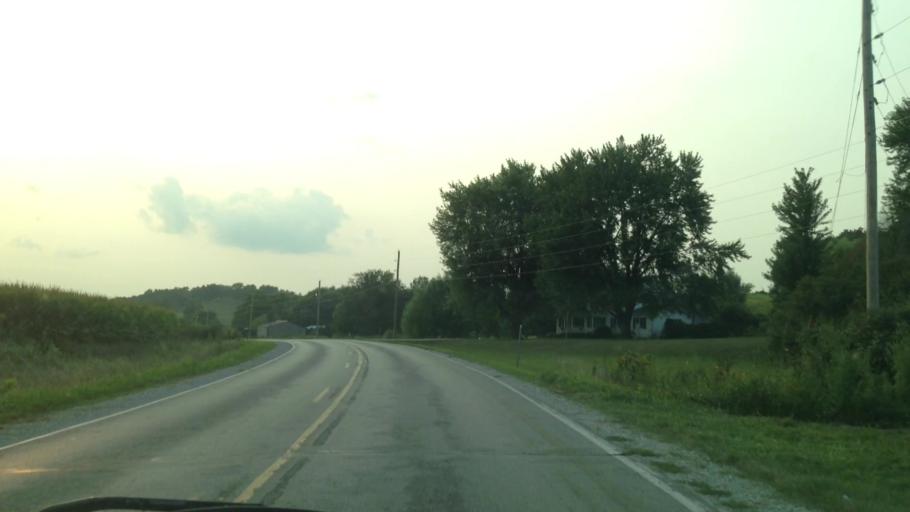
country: US
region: Iowa
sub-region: Iowa County
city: Marengo
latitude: 41.8273
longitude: -92.0740
